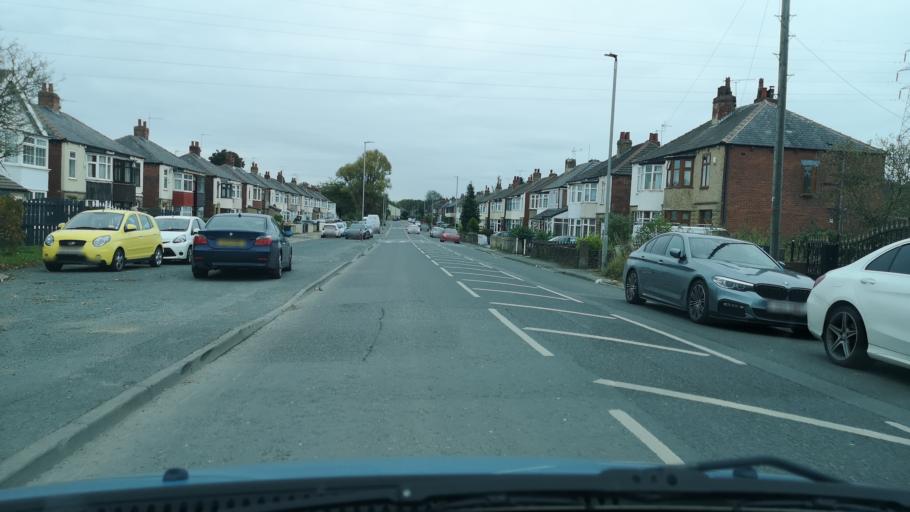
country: GB
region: England
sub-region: Kirklees
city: Dewsbury
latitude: 53.6741
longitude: -1.6515
